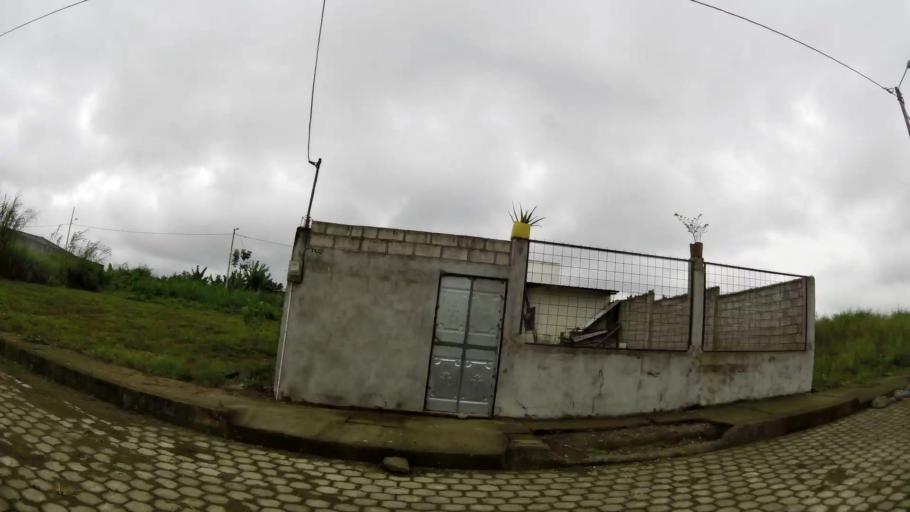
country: EC
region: Santo Domingo de los Tsachilas
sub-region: Canton Santo Domingo de los Colorados
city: Santo Domingo de los Colorados
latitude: -0.2798
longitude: -79.1888
